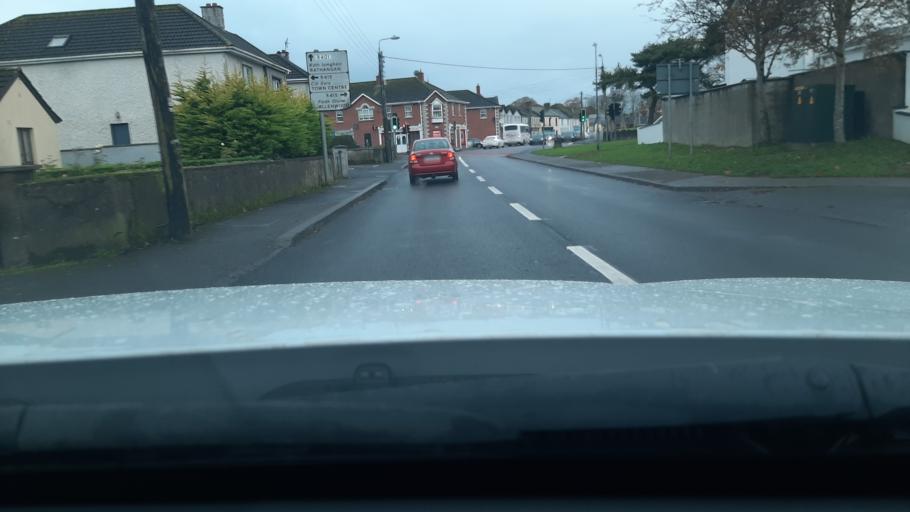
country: IE
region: Leinster
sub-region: Kildare
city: Kildare
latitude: 53.1598
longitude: -6.9078
